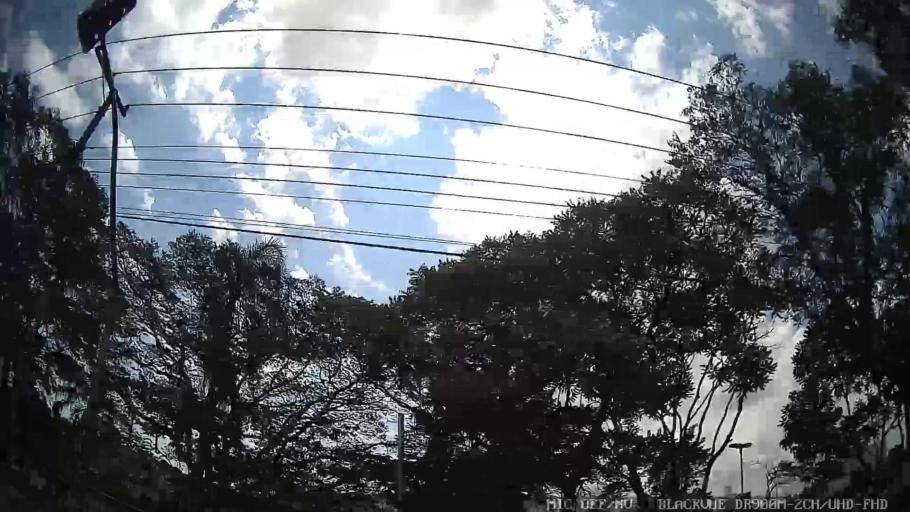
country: BR
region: Sao Paulo
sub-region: Ferraz De Vasconcelos
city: Ferraz de Vasconcelos
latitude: -23.5372
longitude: -46.4550
